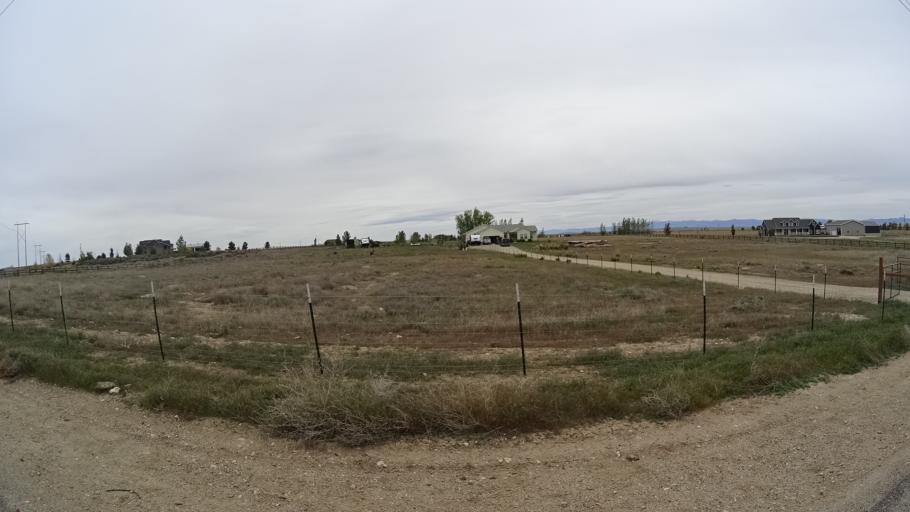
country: US
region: Idaho
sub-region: Ada County
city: Kuna
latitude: 43.4885
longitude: -116.2971
